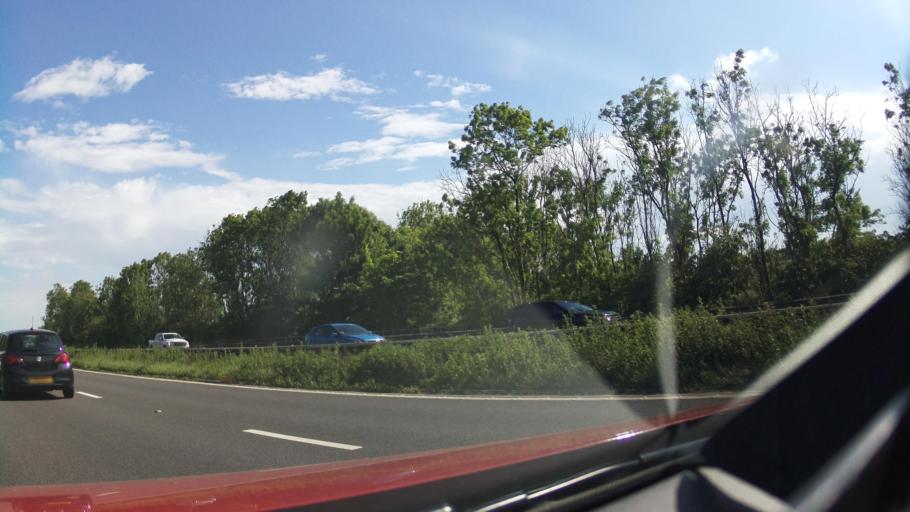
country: GB
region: England
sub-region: Borough of Bolton
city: Horwich
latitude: 53.5898
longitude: -2.5609
